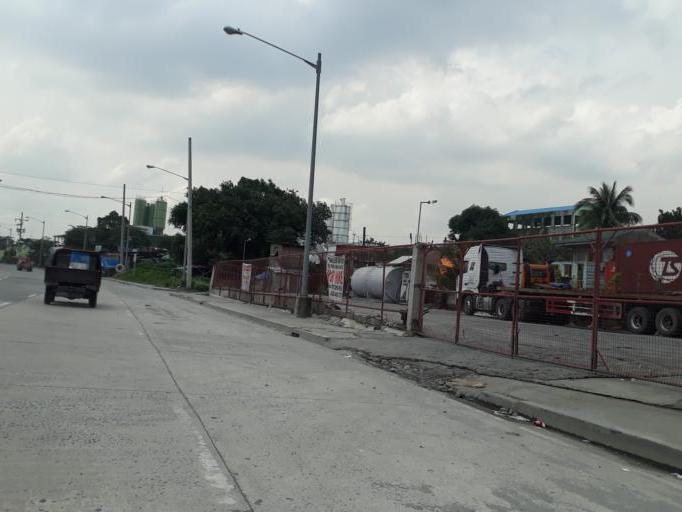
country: PH
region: Calabarzon
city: Bagong Pagasa
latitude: 14.7004
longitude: 121.0159
